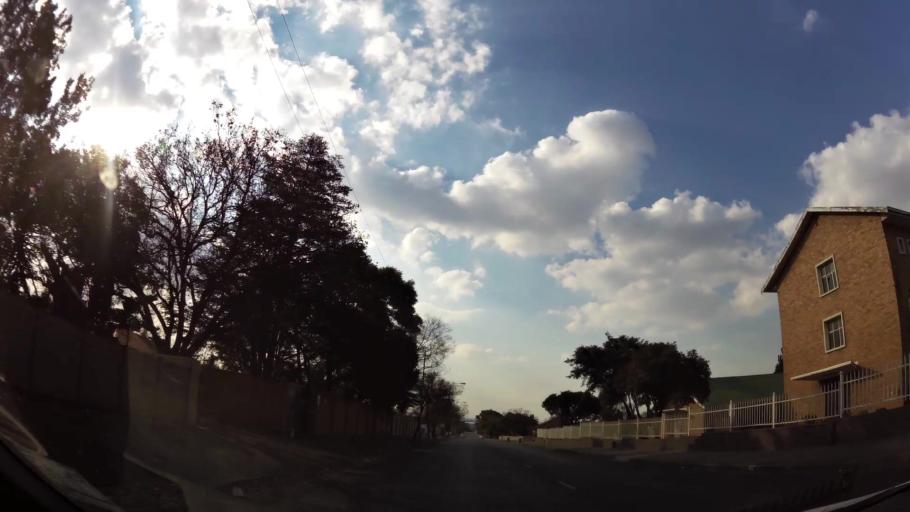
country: ZA
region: Gauteng
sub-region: Ekurhuleni Metropolitan Municipality
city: Germiston
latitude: -26.2394
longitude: 28.1844
